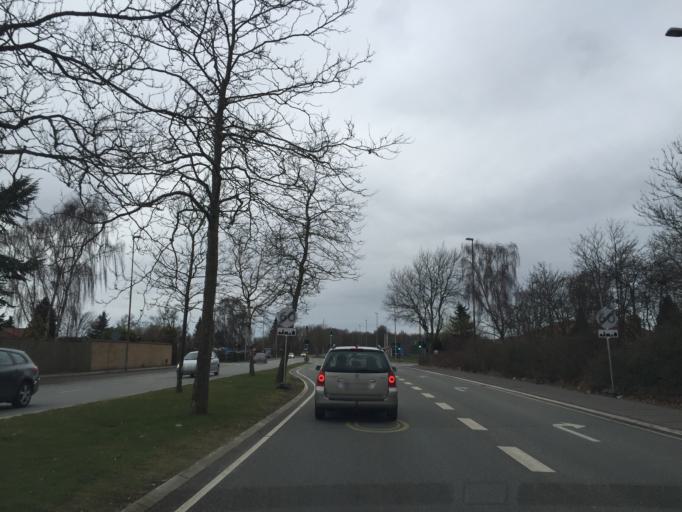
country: DK
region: South Denmark
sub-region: Odense Kommune
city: Odense
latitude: 55.4122
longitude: 10.3405
